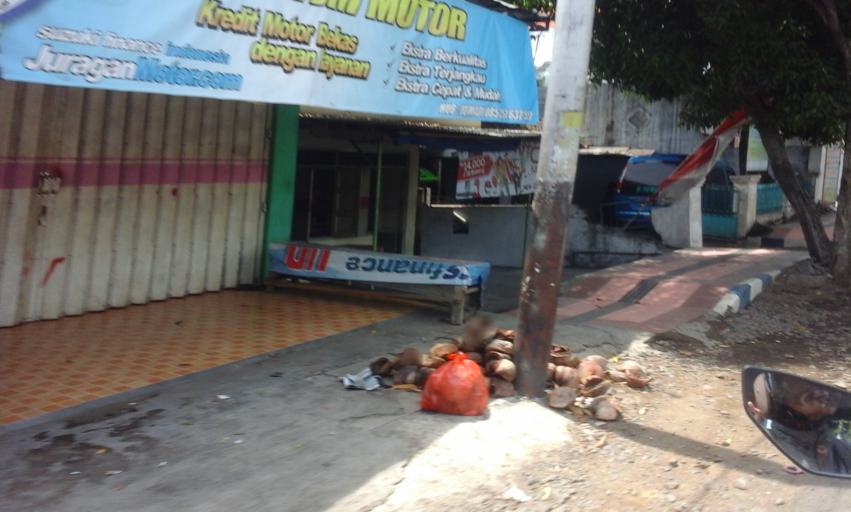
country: ID
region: East Java
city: Kebunjeruk
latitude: -8.1908
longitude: 114.3779
